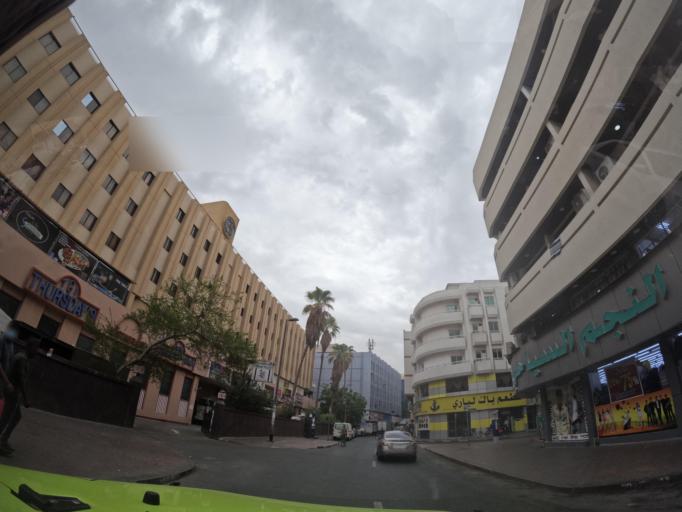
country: AE
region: Ash Shariqah
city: Sharjah
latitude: 25.2624
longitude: 55.2918
